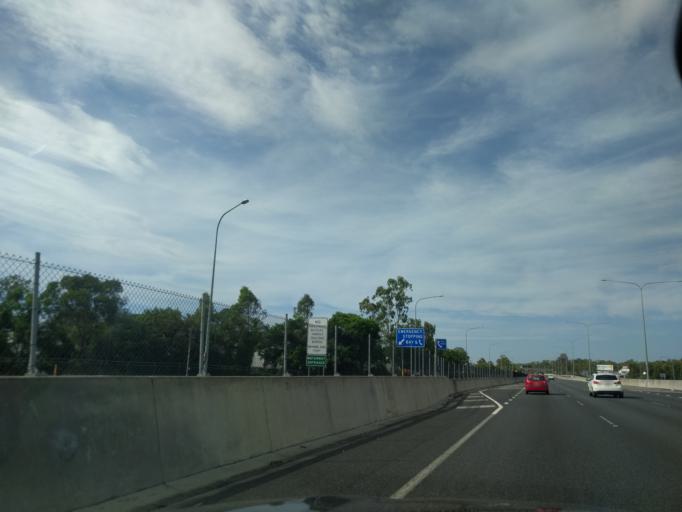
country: AU
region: Queensland
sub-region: Brisbane
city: Wacol
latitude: -27.5892
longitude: 152.9267
